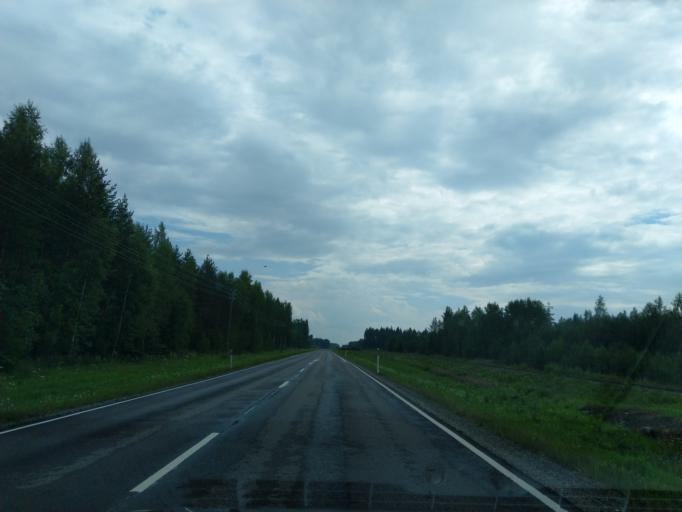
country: FI
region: South Karelia
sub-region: Imatra
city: Parikkala
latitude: 61.6354
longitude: 29.4283
